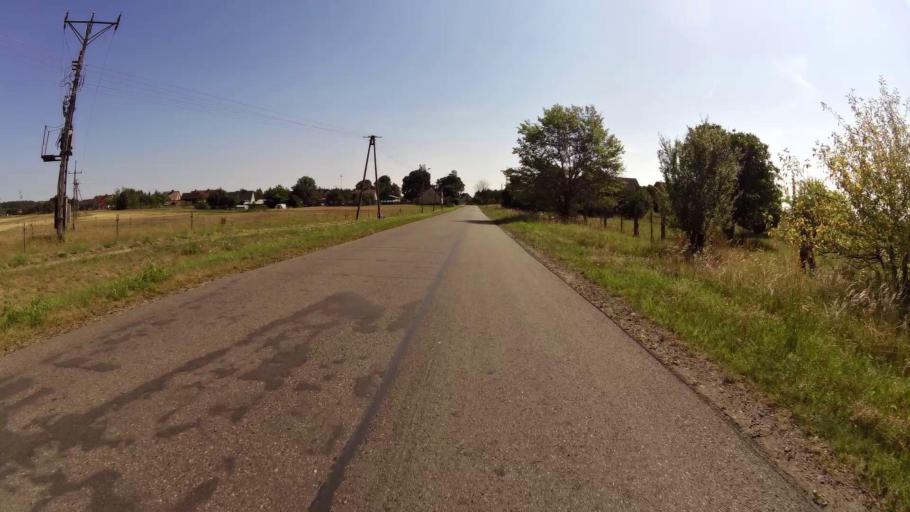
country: PL
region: West Pomeranian Voivodeship
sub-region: Powiat drawski
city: Czaplinek
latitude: 53.4434
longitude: 16.2640
